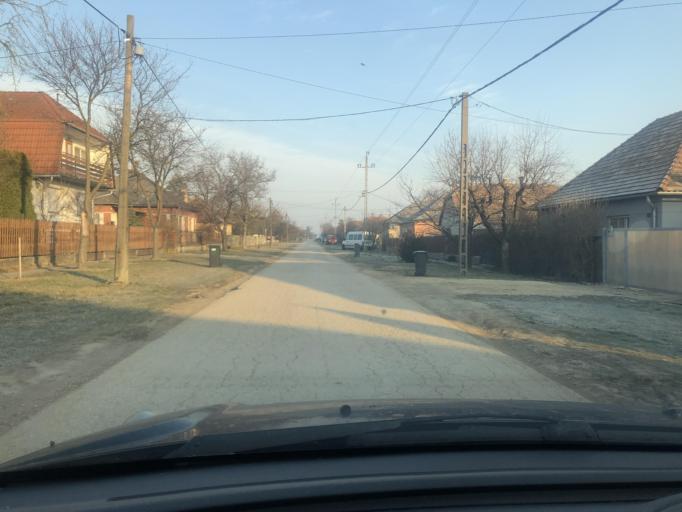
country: HU
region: Fejer
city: Lovasbereny
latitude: 47.3166
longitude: 18.5481
